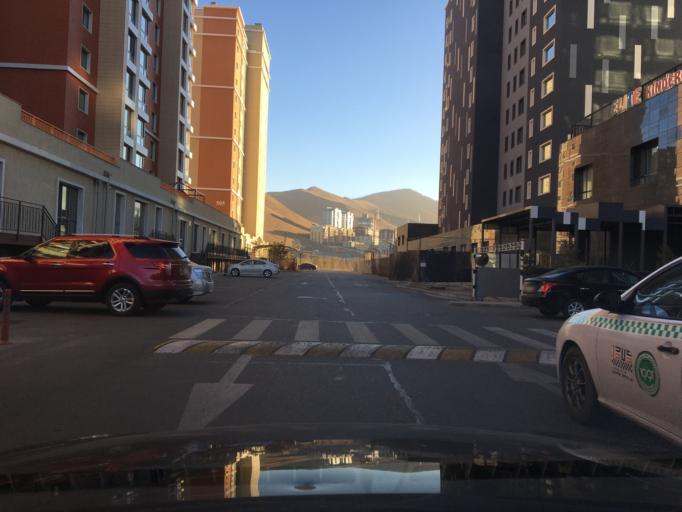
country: MN
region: Ulaanbaatar
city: Ulaanbaatar
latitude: 47.8914
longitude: 106.9237
